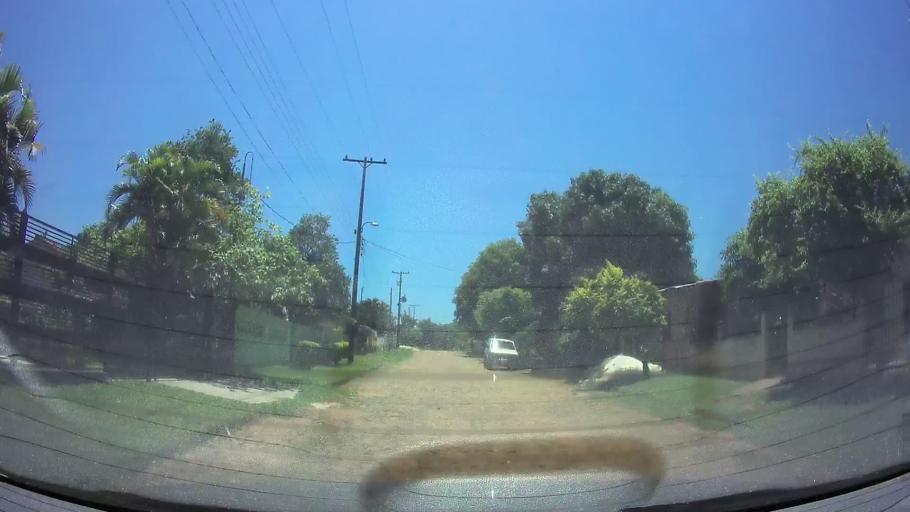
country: PY
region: Central
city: Limpio
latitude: -25.2426
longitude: -57.4865
